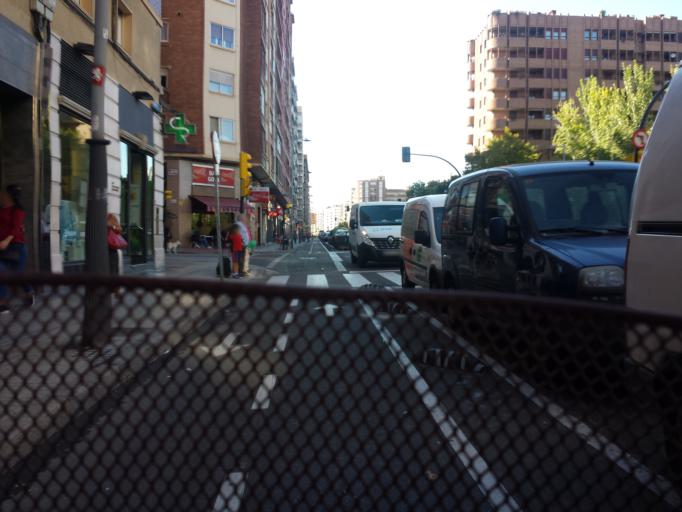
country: ES
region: Aragon
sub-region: Provincia de Zaragoza
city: Zaragoza
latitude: 41.6394
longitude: -0.8804
